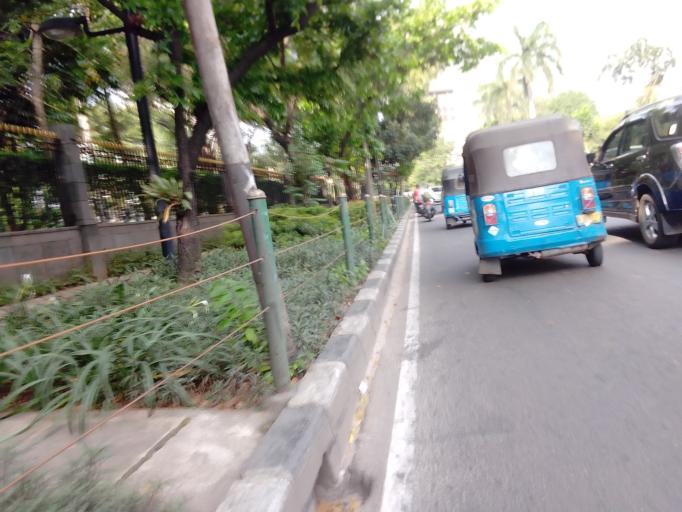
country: ID
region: Jakarta Raya
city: Jakarta
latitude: -6.1831
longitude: 106.8209
